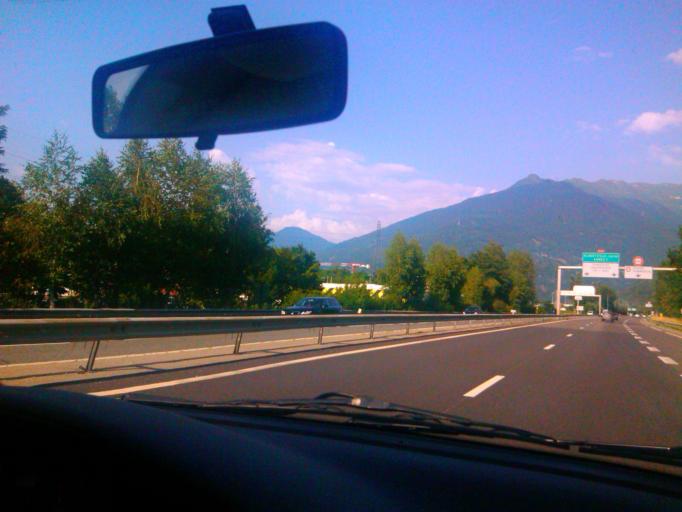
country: FR
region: Rhone-Alpes
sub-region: Departement de la Savoie
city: Frontenex
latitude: 45.6265
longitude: 6.3251
